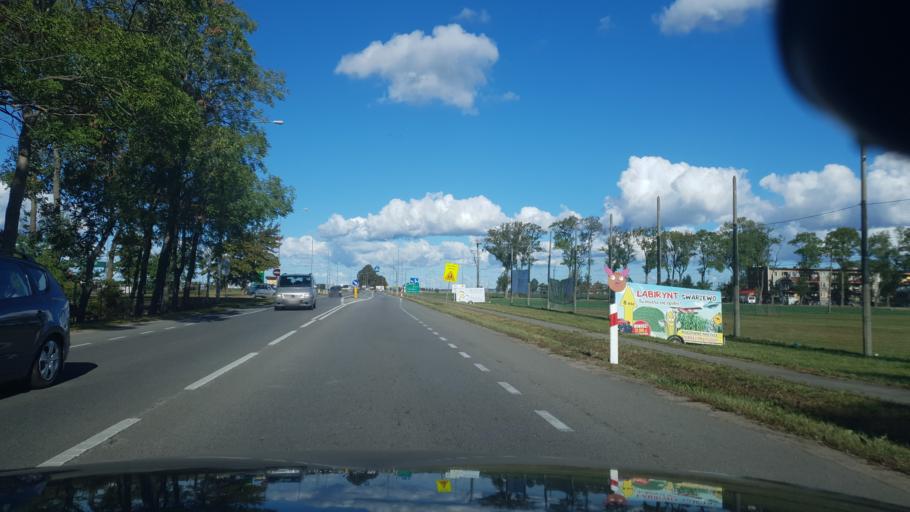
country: PL
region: Pomeranian Voivodeship
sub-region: Powiat pucki
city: Zelistrzewo
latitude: 54.6842
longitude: 18.3705
